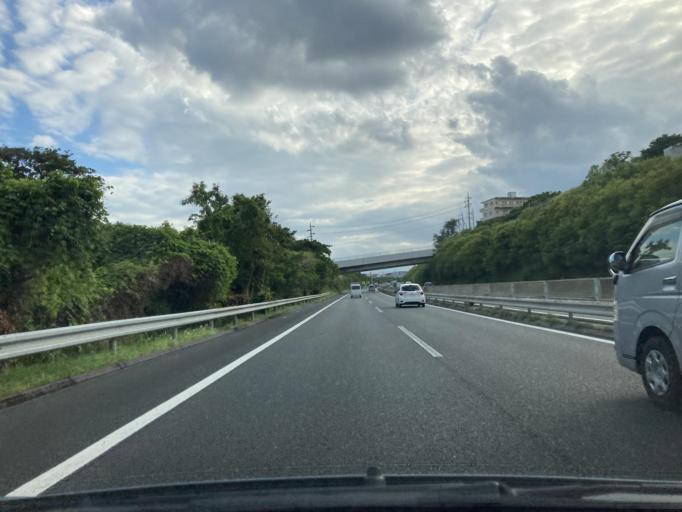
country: JP
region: Okinawa
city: Ginowan
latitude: 26.2661
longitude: 127.7742
